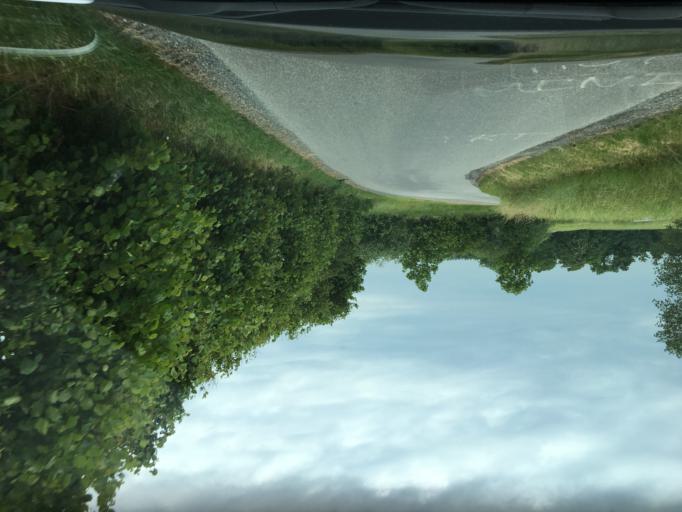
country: DK
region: South Denmark
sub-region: Vejle Kommune
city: Vejle
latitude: 55.6164
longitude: 9.5498
